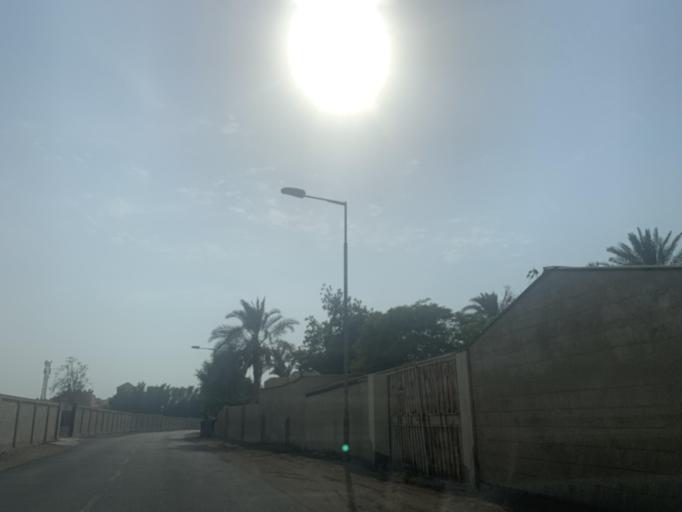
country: BH
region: Manama
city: Jidd Hafs
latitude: 26.2156
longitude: 50.4937
